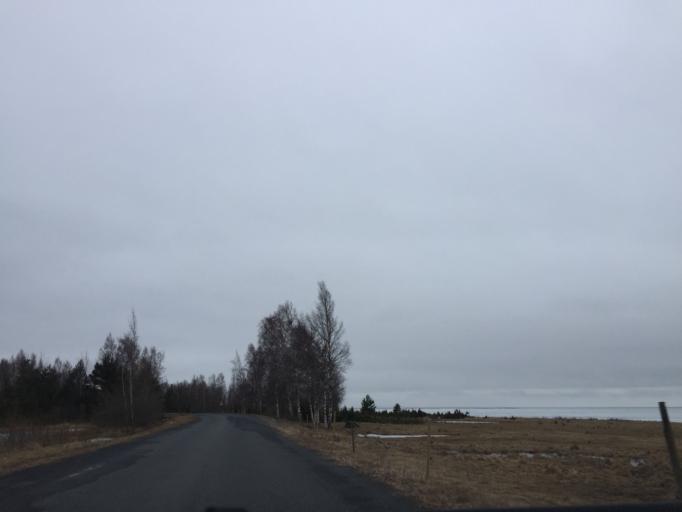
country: EE
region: Laeaene
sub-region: Haapsalu linn
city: Haapsalu
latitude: 58.7777
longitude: 23.4628
